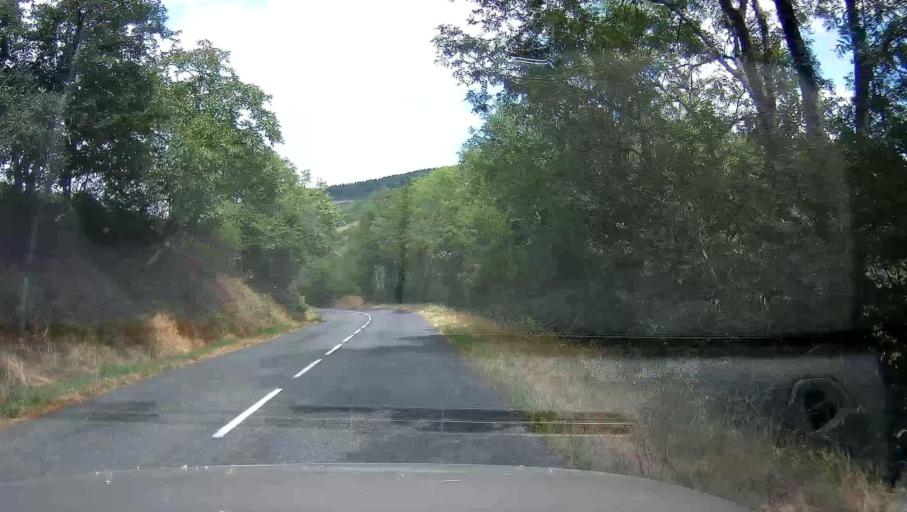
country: FR
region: Rhone-Alpes
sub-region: Departement du Rhone
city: Le Perreon
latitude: 46.0166
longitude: 4.5830
